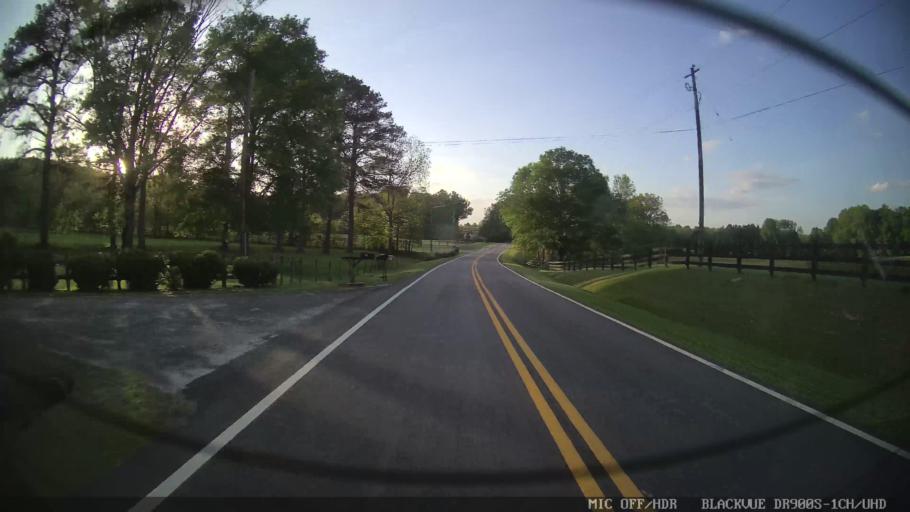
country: US
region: Georgia
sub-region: Bartow County
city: Emerson
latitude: 34.1117
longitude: -84.7918
